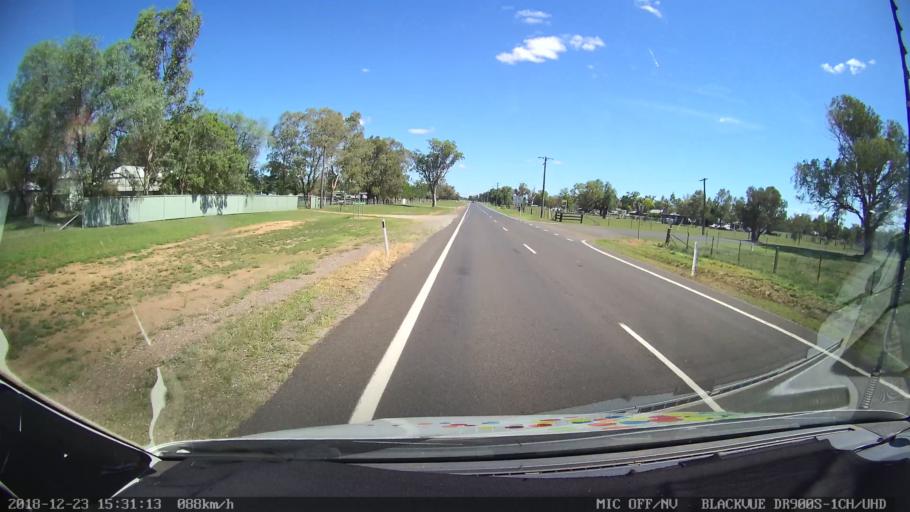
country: AU
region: New South Wales
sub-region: Tamworth Municipality
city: East Tamworth
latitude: -30.9691
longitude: 150.8667
